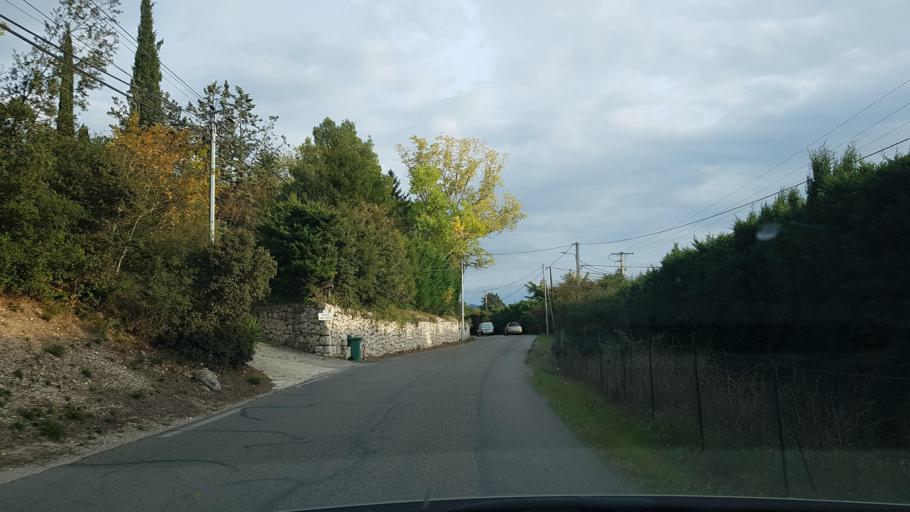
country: FR
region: Provence-Alpes-Cote d'Azur
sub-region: Departement des Bouches-du-Rhone
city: Cabries
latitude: 43.4484
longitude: 5.3664
